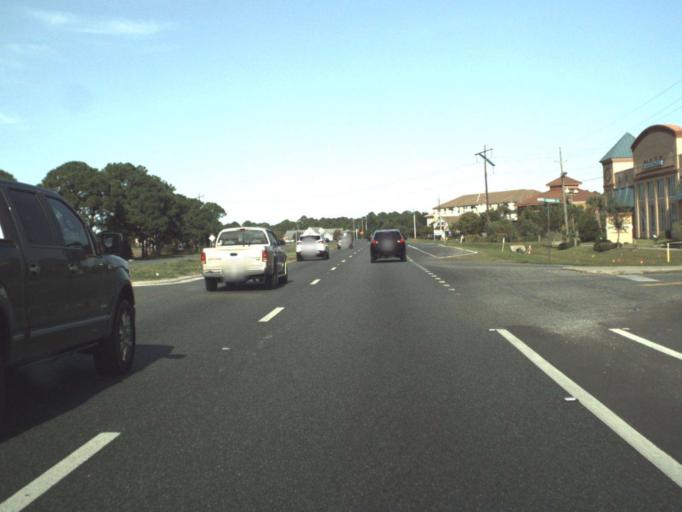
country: US
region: Florida
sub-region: Walton County
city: Miramar Beach
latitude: 30.3831
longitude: -86.3604
